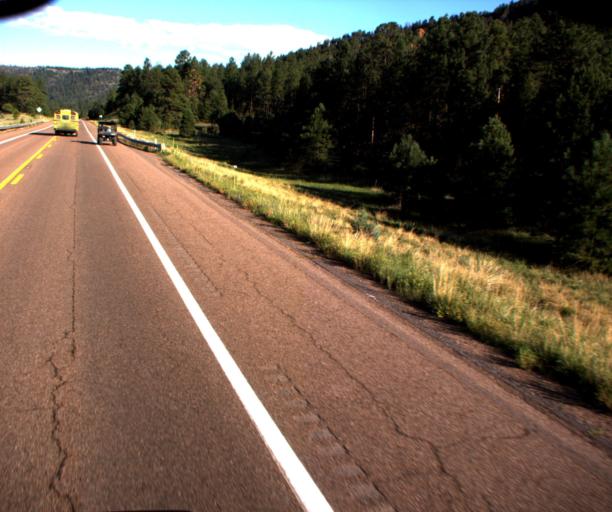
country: US
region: Arizona
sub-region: Apache County
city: Eagar
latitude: 33.8554
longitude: -109.1539
